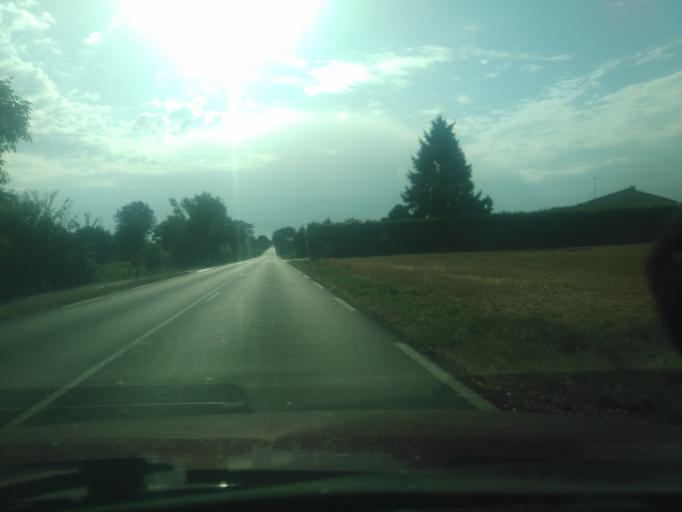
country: FR
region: Pays de la Loire
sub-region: Departement de la Vendee
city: Bazoges-en-Pareds
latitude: 46.6799
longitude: -0.9559
